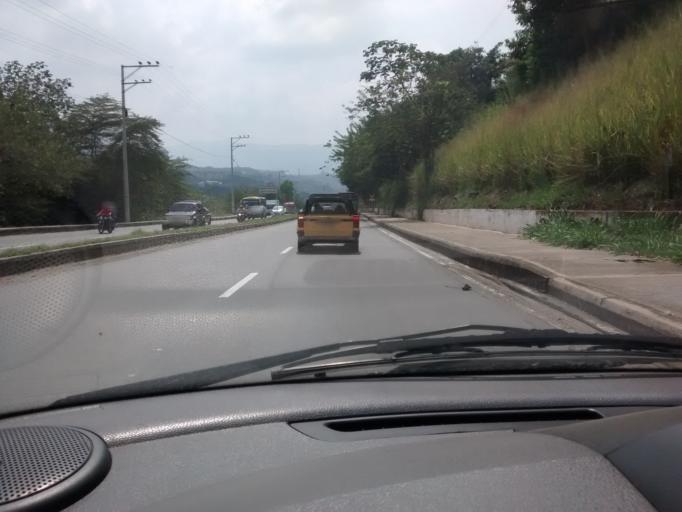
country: CO
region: Santander
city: Bucaramanga
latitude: 7.0958
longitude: -73.1168
